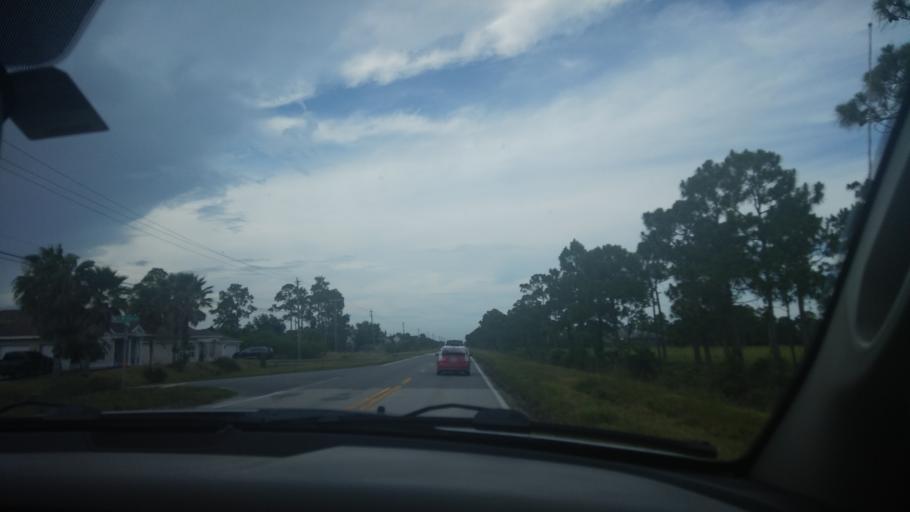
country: US
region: Florida
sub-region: Brevard County
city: Grant-Valkaria
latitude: 27.9113
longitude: -80.6231
